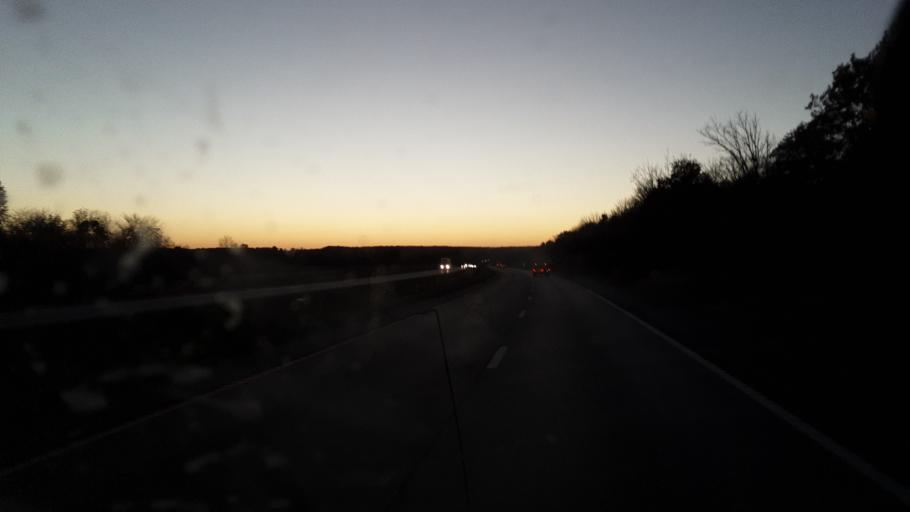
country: US
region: Missouri
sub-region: Callaway County
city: Fulton
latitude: 38.9386
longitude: -91.8288
